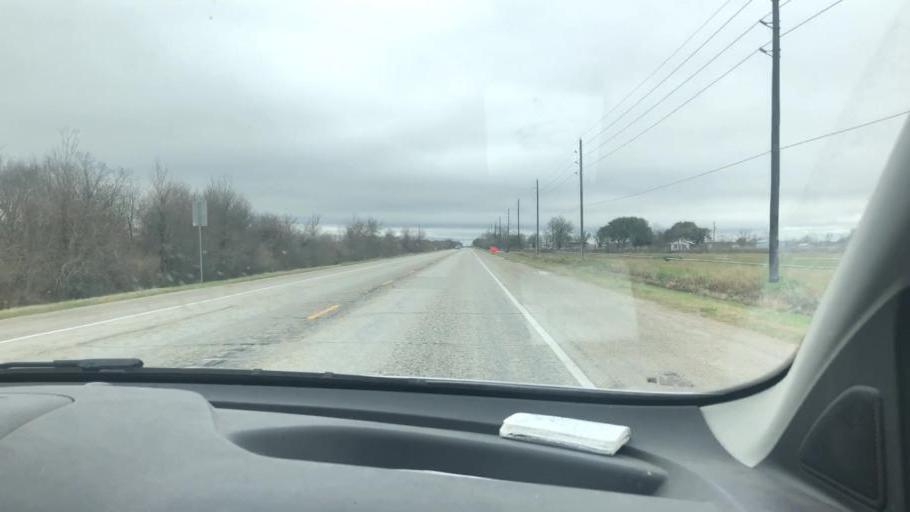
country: US
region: Texas
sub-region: Wharton County
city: Wharton
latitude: 29.2721
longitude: -96.0608
